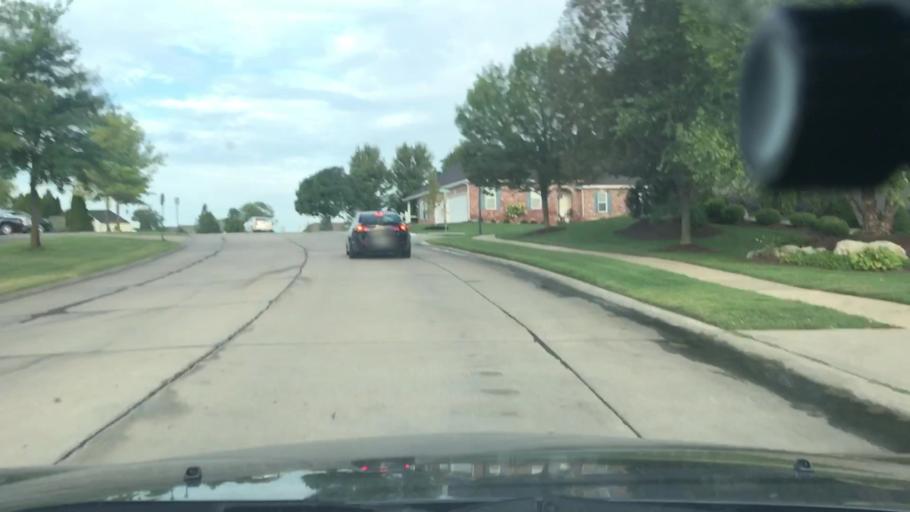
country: US
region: Missouri
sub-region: Saint Charles County
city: Wentzville
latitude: 38.8187
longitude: -90.8959
